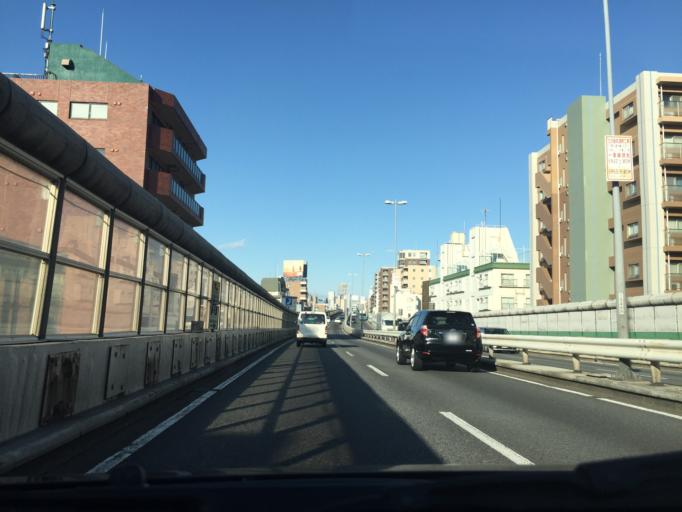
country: JP
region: Tokyo
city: Tokyo
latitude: 35.6274
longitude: 139.6450
